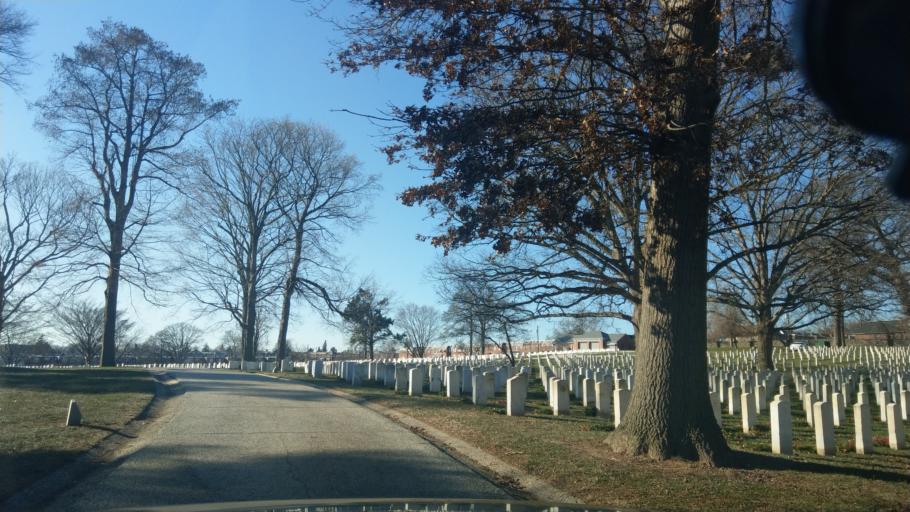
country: US
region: Pennsylvania
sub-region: Montgomery County
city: Wyncote
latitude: 40.0587
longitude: -75.1532
